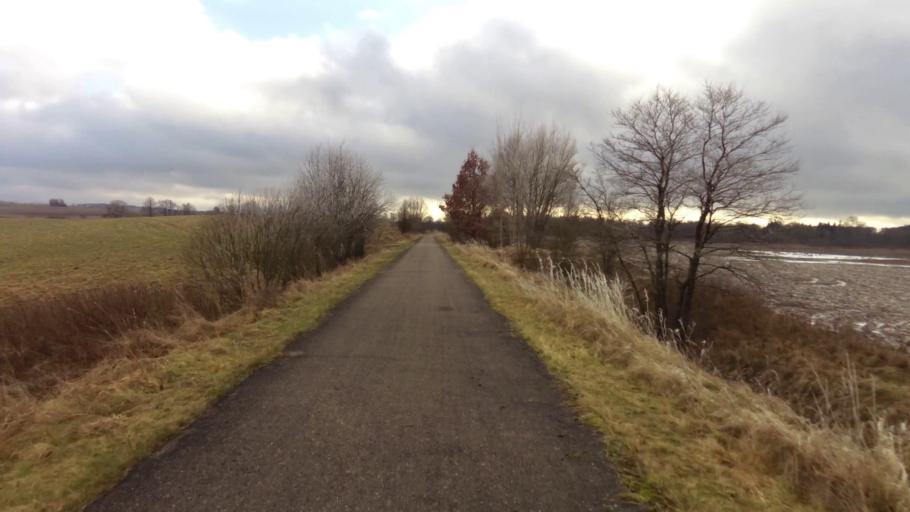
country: PL
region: West Pomeranian Voivodeship
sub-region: Powiat drawski
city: Zlocieniec
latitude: 53.6256
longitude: 16.0568
